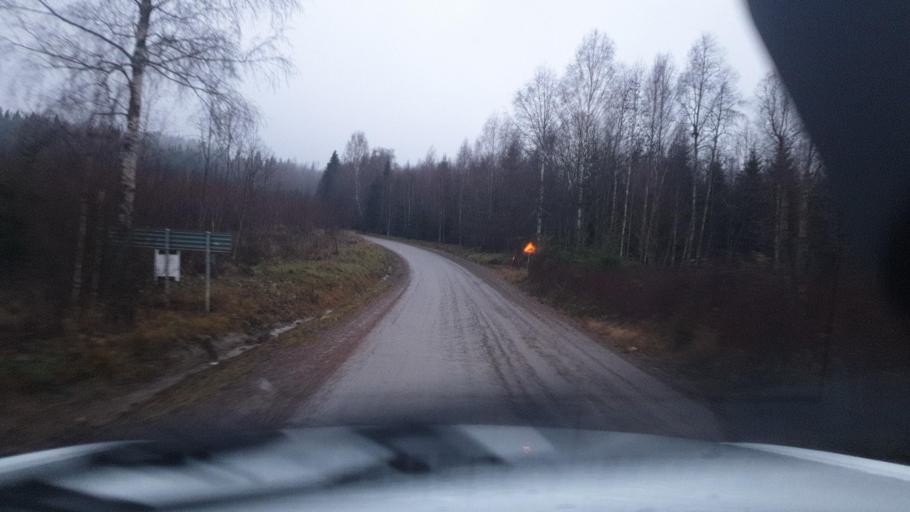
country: SE
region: Vaermland
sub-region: Sunne Kommun
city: Sunne
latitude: 59.8461
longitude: 12.9411
